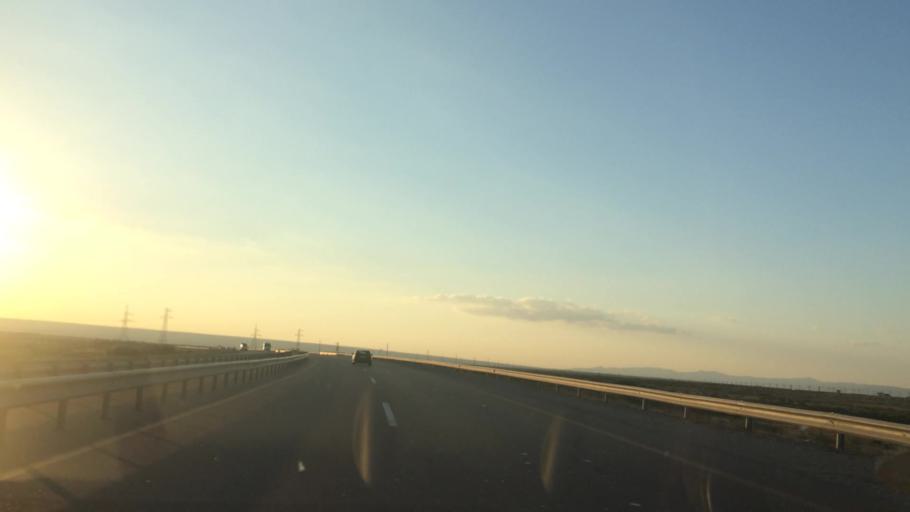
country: AZ
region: Baki
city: Qobustan
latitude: 39.9825
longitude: 49.2309
